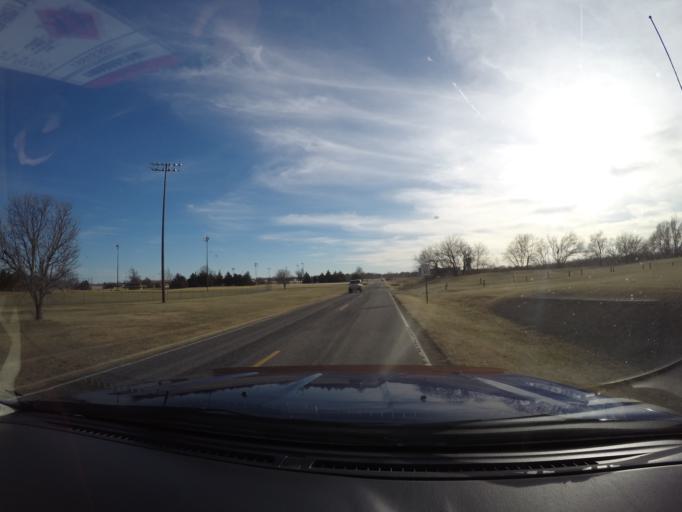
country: US
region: Kansas
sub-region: Harvey County
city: North Newton
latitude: 38.0640
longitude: -97.3368
